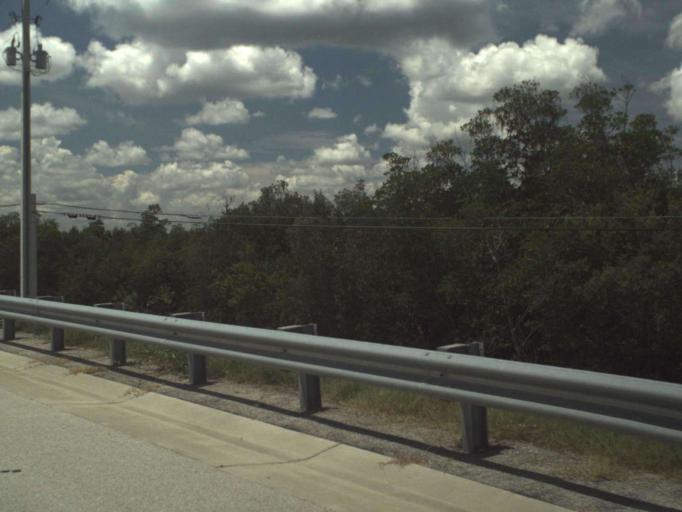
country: US
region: Florida
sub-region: Saint Lucie County
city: Indian River Estates
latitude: 27.3791
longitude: -80.2560
